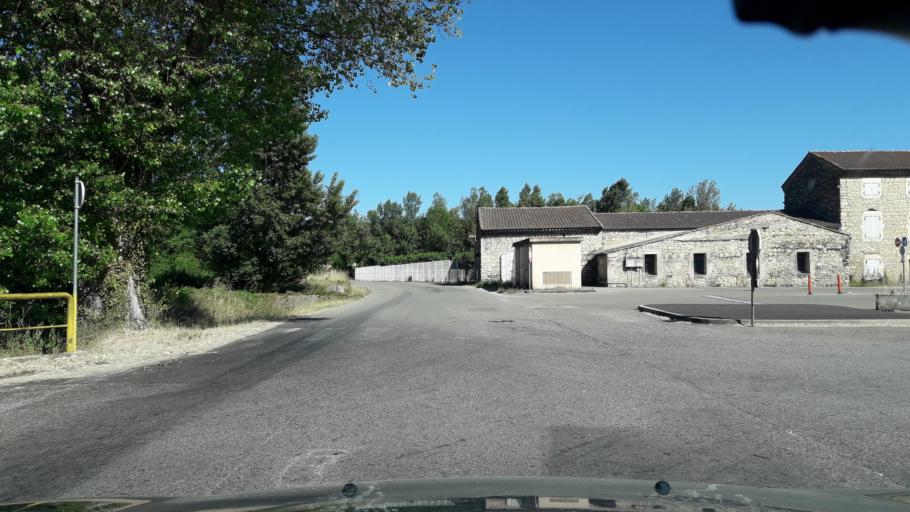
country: FR
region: Rhone-Alpes
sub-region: Departement de la Drome
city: Loriol-sur-Drome
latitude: 44.7478
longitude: 4.8002
